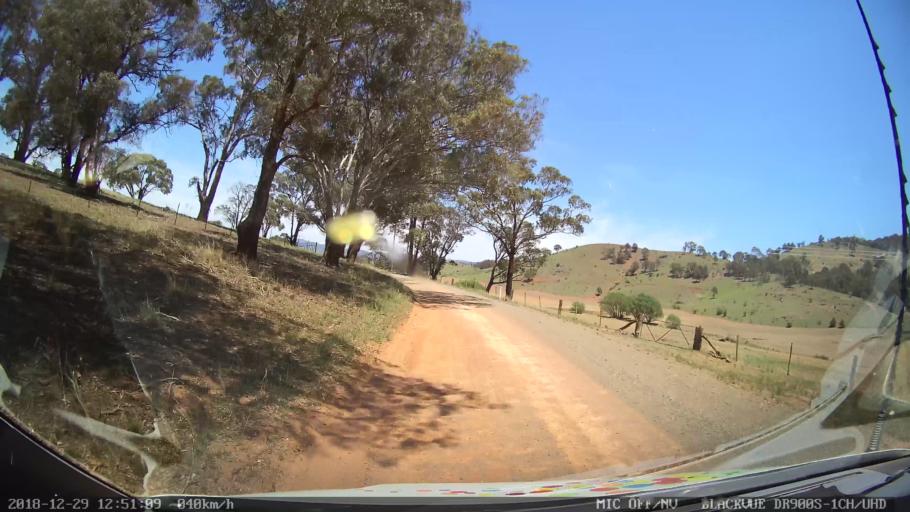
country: AU
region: Australian Capital Territory
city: Macarthur
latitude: -35.6733
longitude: 149.2001
